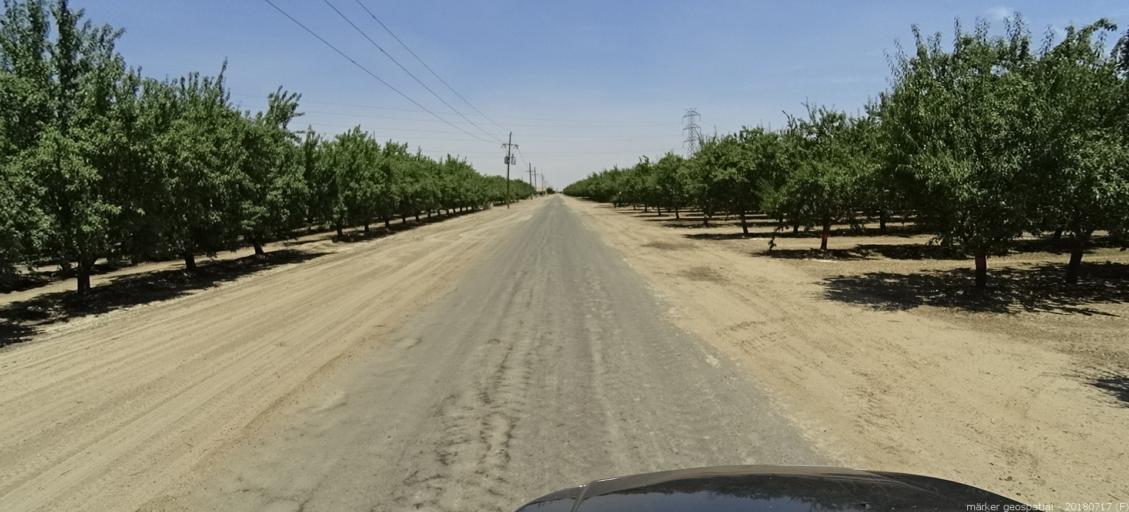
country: US
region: California
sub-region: Madera County
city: Fairmead
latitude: 37.0691
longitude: -120.1436
